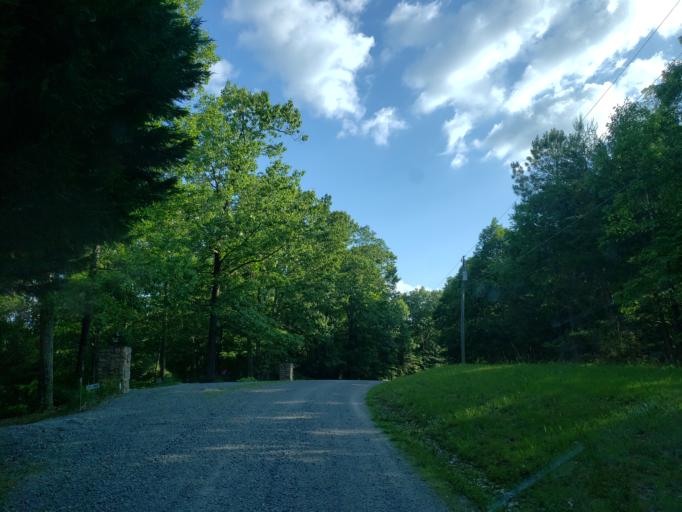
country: US
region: Georgia
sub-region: Murray County
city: Chatsworth
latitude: 34.6476
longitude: -84.6481
